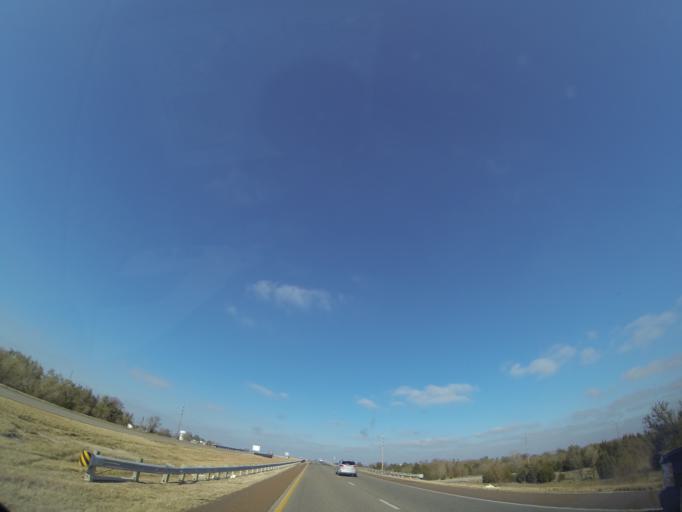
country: US
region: Kansas
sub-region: McPherson County
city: McPherson
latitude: 38.3759
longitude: -97.6205
